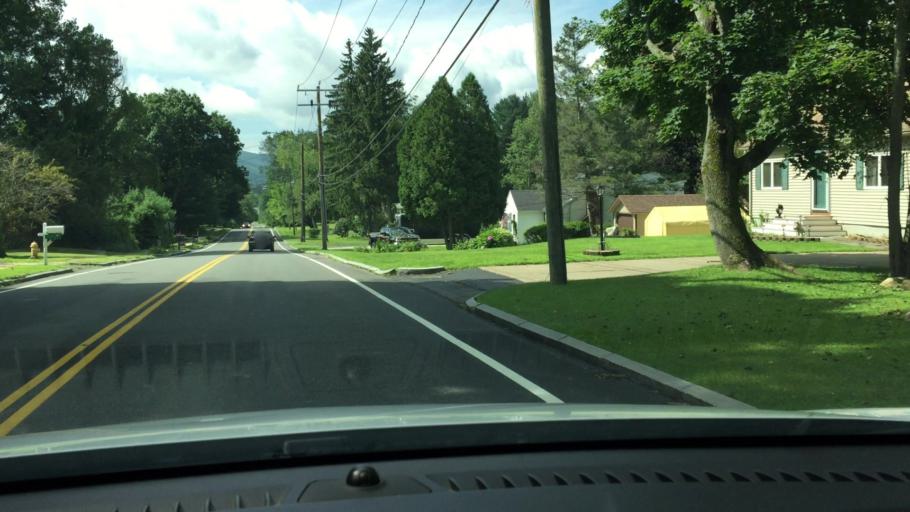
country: US
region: Massachusetts
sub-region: Berkshire County
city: Pittsfield
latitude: 42.4542
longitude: -73.2984
